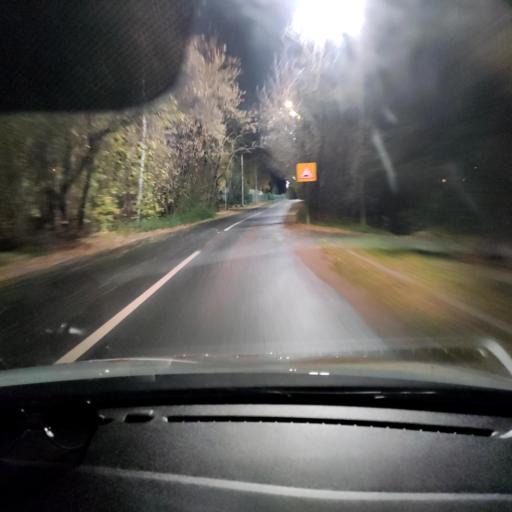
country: RU
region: Tatarstan
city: Verkhniy Uslon
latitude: 55.6236
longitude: 49.0138
